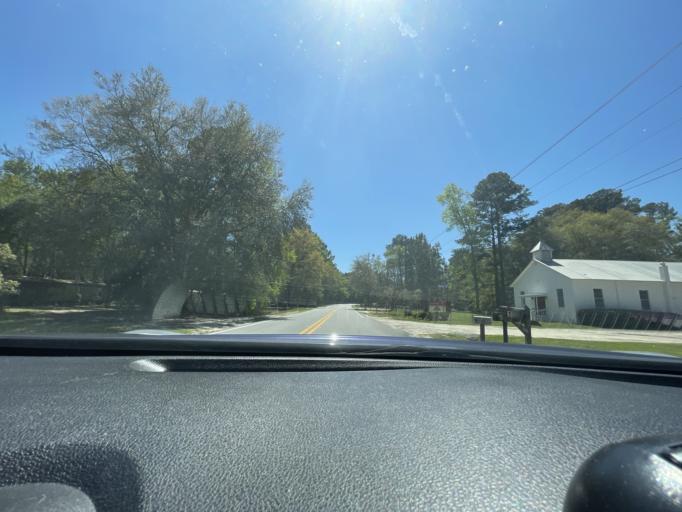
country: US
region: Georgia
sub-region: Chatham County
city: Pooler
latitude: 32.0932
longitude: -81.2403
